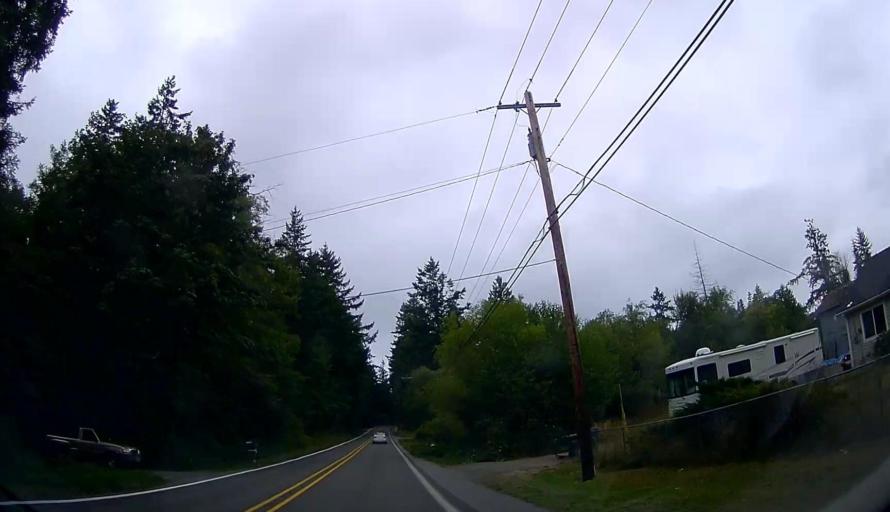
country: US
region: Washington
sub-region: Snohomish County
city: Tulalip
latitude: 48.1103
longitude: -122.3409
